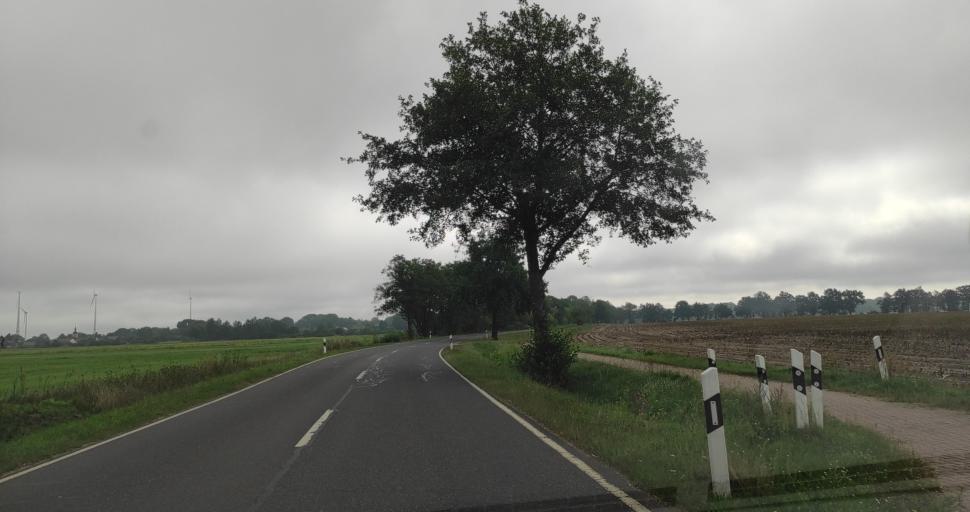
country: DE
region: Brandenburg
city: Forst
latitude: 51.6903
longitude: 14.6125
